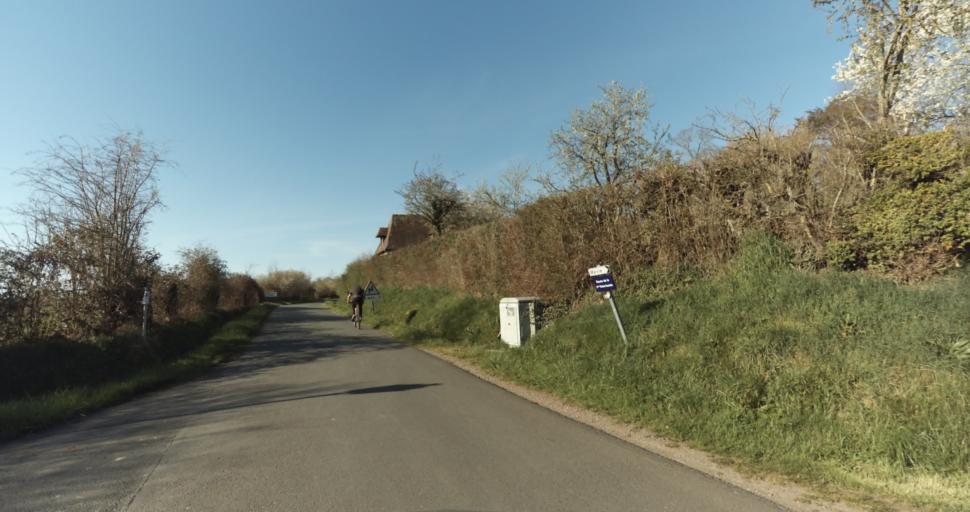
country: FR
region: Lower Normandy
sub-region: Departement du Calvados
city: Saint-Pierre-sur-Dives
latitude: 49.0401
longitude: 0.0398
